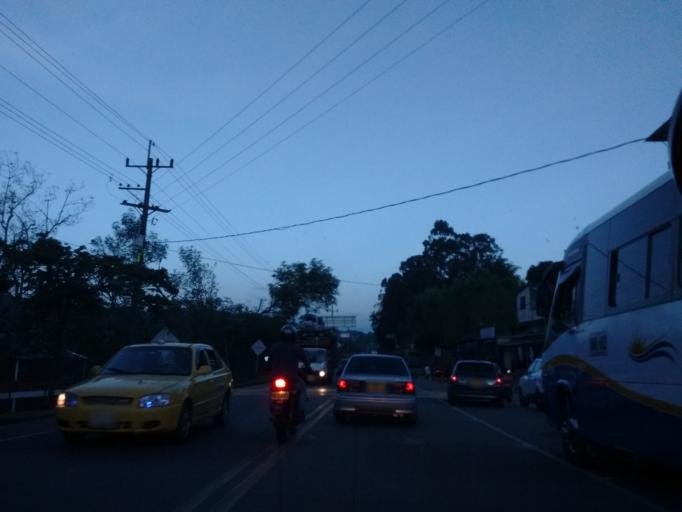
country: CO
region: Antioquia
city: Santuario
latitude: 6.1346
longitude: -75.2634
